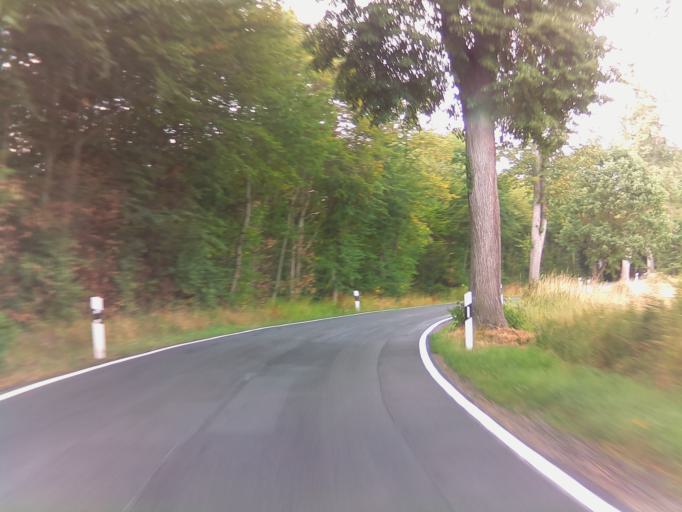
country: DE
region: Hesse
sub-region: Regierungsbezirk Giessen
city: Lauterbach
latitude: 50.5717
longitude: 9.4324
